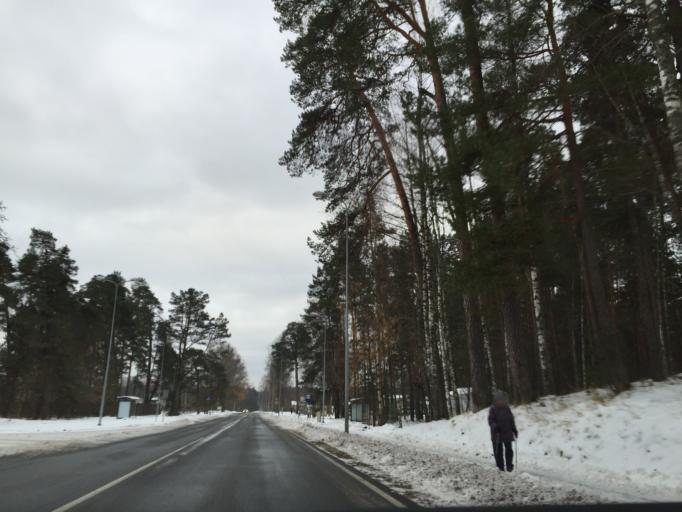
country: LV
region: Saulkrastu
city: Saulkrasti
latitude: 57.2348
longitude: 24.3942
